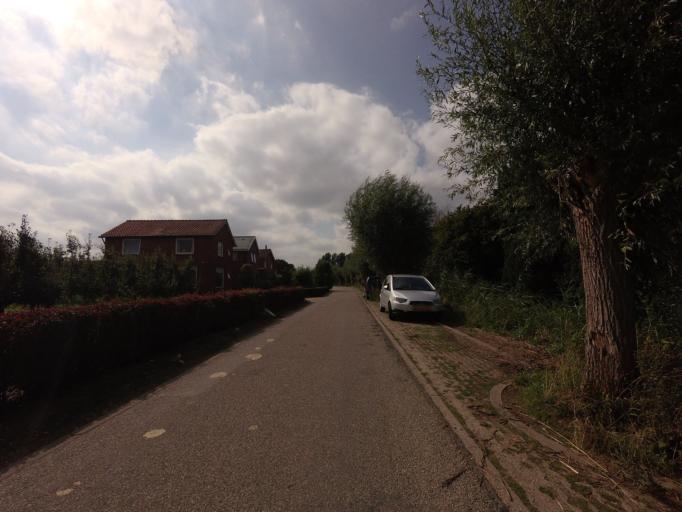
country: NL
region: Utrecht
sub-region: Gemeente Utrecht
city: Lunetten
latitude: 52.0497
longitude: 5.1333
